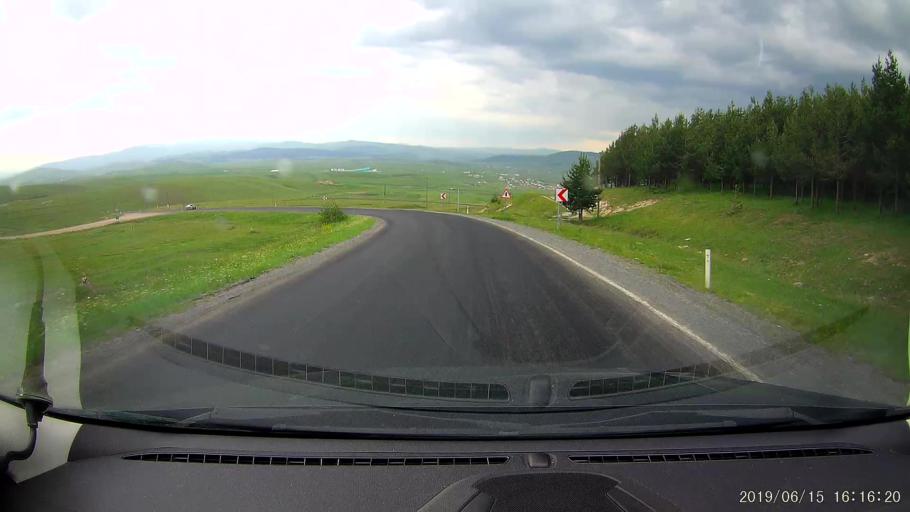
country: TR
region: Ardahan
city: Hanak
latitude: 41.2596
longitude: 42.8524
